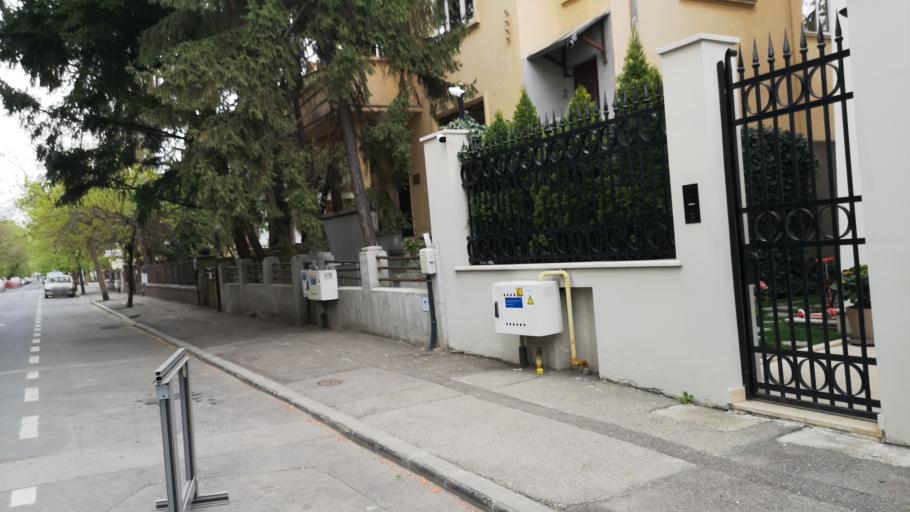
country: RO
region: Bucuresti
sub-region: Municipiul Bucuresti
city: Bucharest
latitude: 44.4619
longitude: 26.0875
